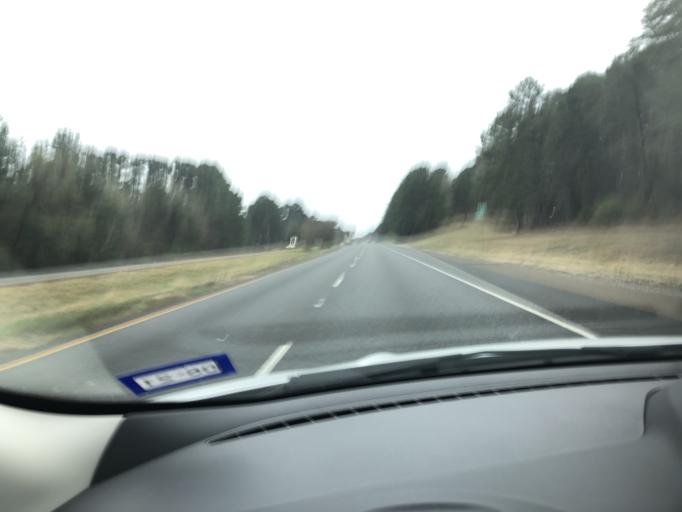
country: US
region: Texas
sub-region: Nacogdoches County
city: Nacogdoches
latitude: 31.5464
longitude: -94.6890
